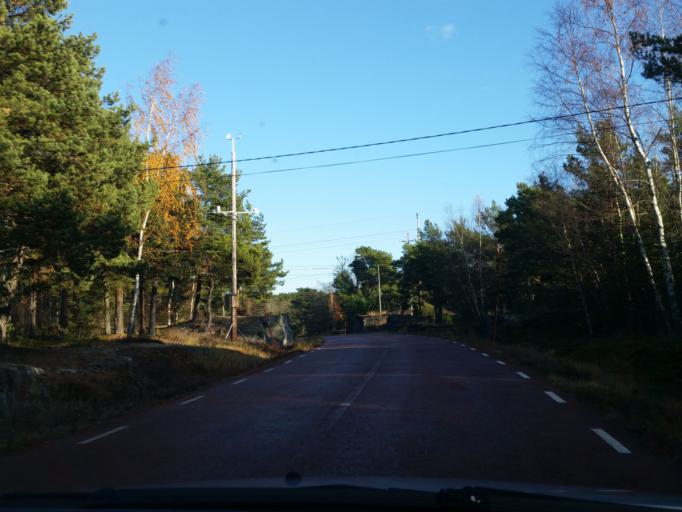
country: AX
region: Alands skaergard
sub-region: Braendoe
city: Braendoe
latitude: 60.4634
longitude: 21.0811
